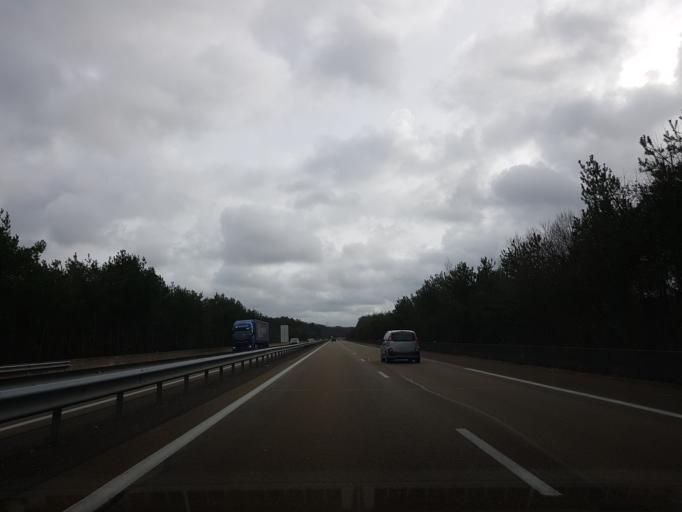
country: FR
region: Champagne-Ardenne
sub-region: Departement de la Haute-Marne
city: Chamarandes-Choignes
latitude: 48.0056
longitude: 5.1101
